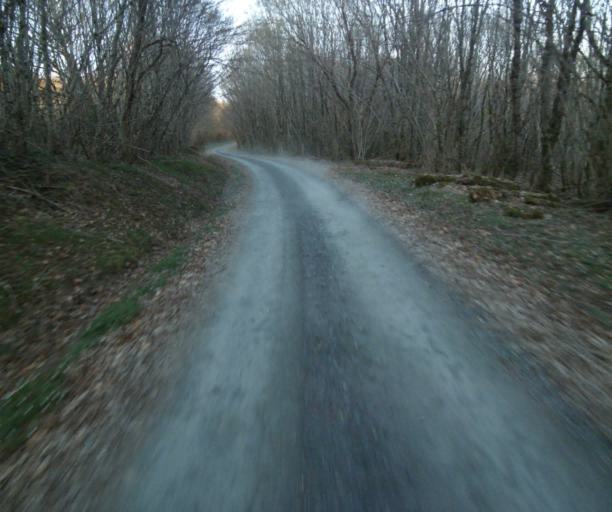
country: FR
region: Limousin
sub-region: Departement de la Correze
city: Uzerche
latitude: 45.3545
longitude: 1.6022
